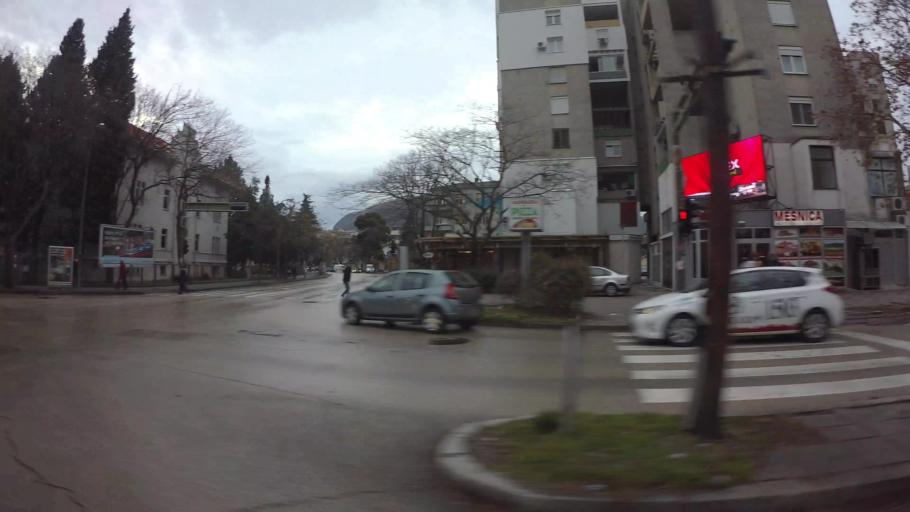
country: BA
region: Federation of Bosnia and Herzegovina
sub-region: Hercegovacko-Bosanski Kanton
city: Mostar
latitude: 43.3478
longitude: 17.8042
